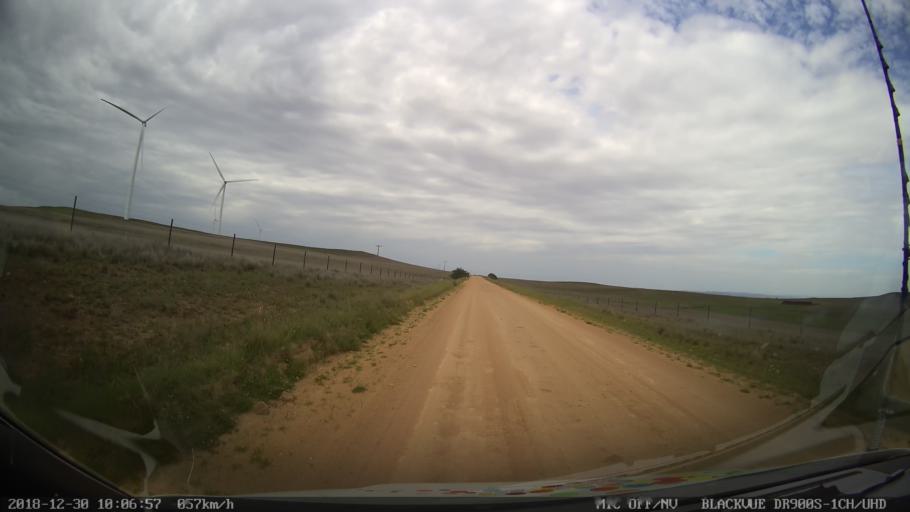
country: AU
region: New South Wales
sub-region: Cooma-Monaro
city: Cooma
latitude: -36.5361
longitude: 149.1262
